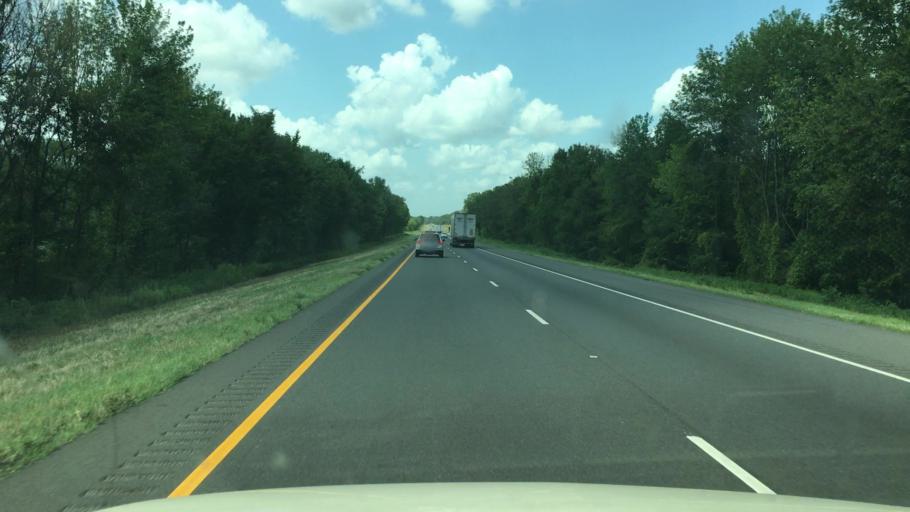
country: US
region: Arkansas
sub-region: Hempstead County
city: Hope
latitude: 33.7285
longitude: -93.5400
